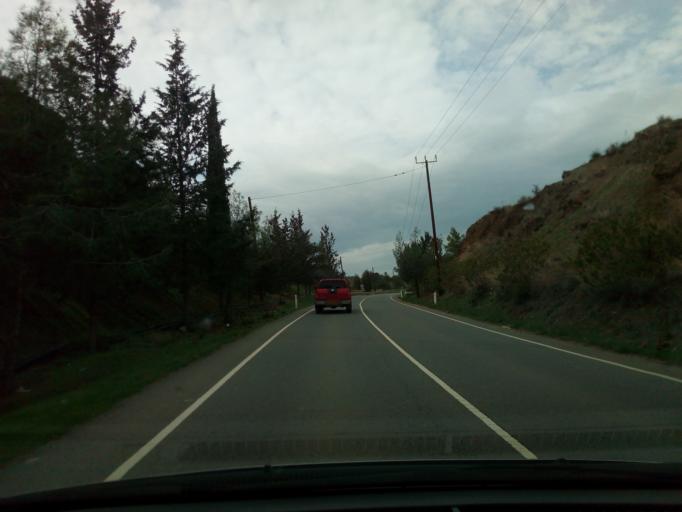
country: CY
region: Lefkosia
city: Lefka
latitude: 35.0749
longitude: 32.8997
